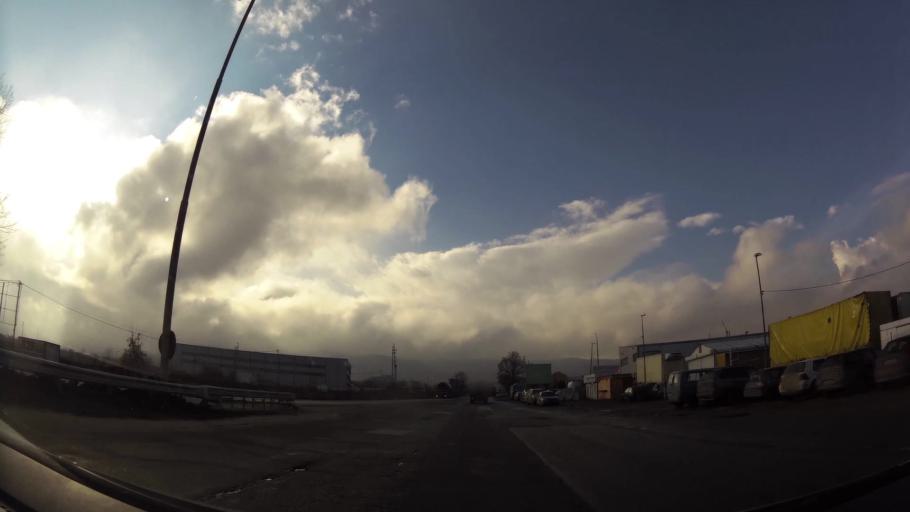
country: BG
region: Sofia-Capital
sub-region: Stolichna Obshtina
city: Sofia
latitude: 42.6286
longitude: 23.4465
